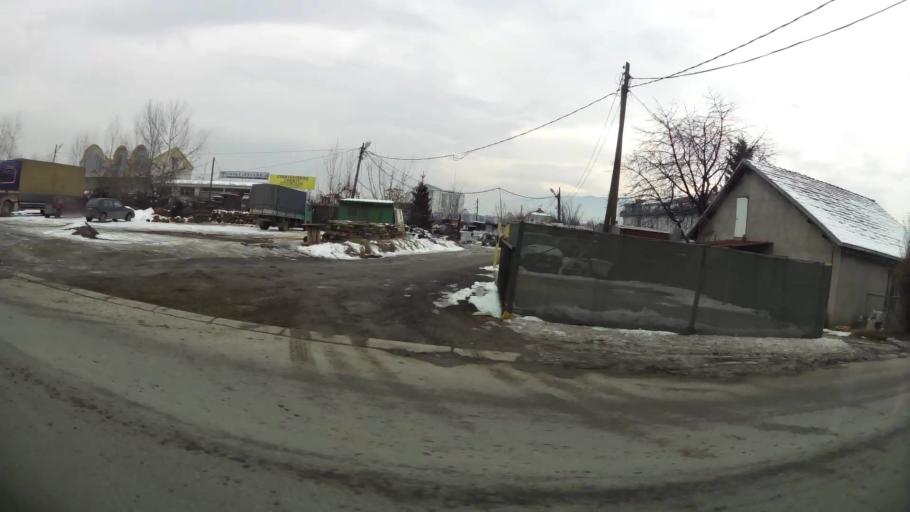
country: MK
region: Butel
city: Butel
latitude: 42.0280
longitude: 21.4415
